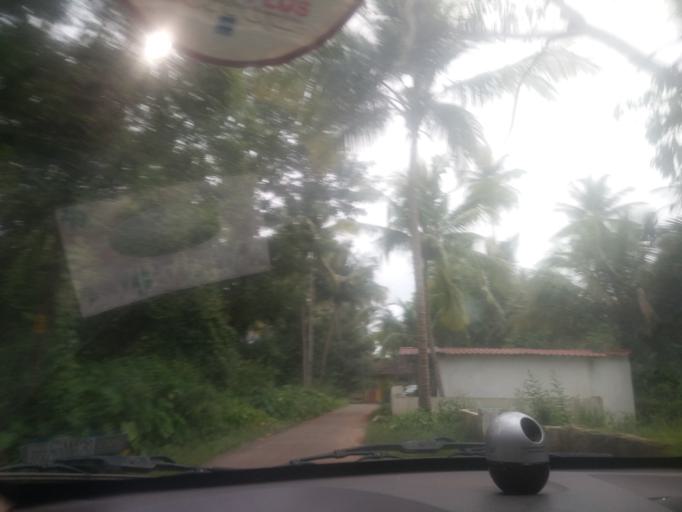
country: IN
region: Goa
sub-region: South Goa
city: Cuncolim
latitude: 15.1777
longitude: 73.9695
